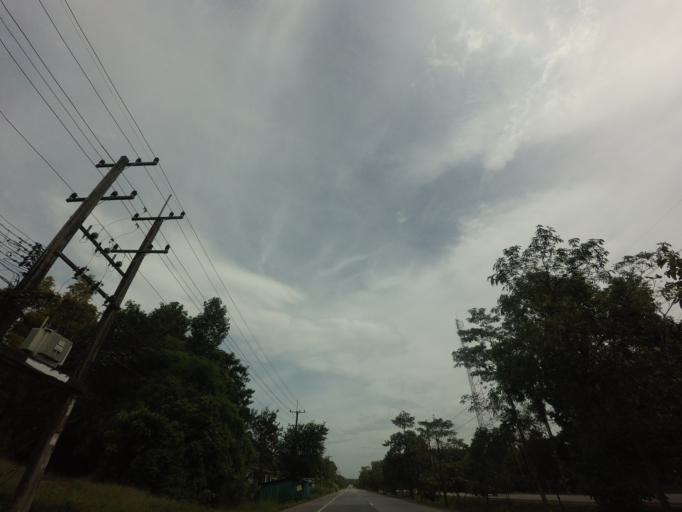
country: TH
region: Rayong
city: Klaeng
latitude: 12.6911
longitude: 101.5365
